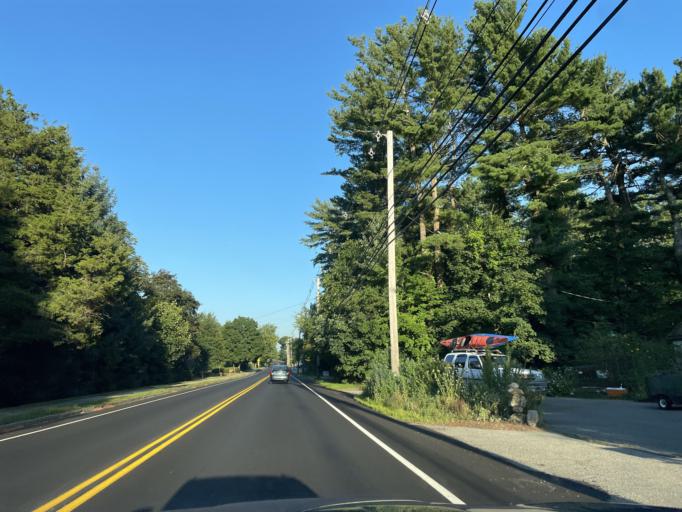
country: US
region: Massachusetts
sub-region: Plymouth County
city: Halifax
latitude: 41.9923
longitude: -70.8672
